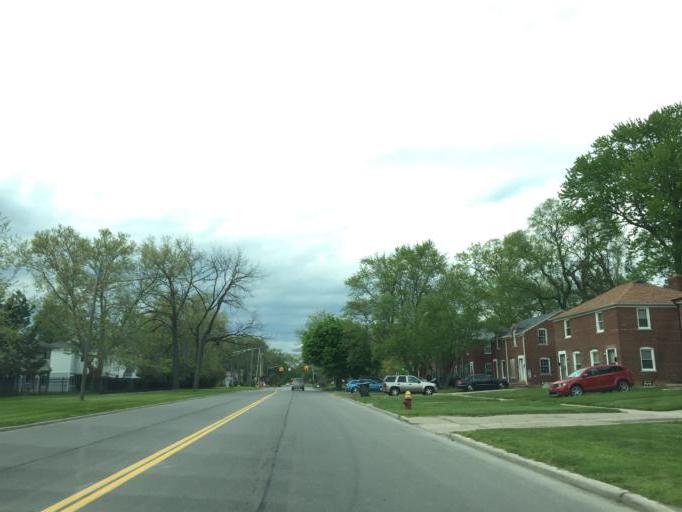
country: US
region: Michigan
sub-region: Wayne County
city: Redford
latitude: 42.3918
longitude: -83.2370
